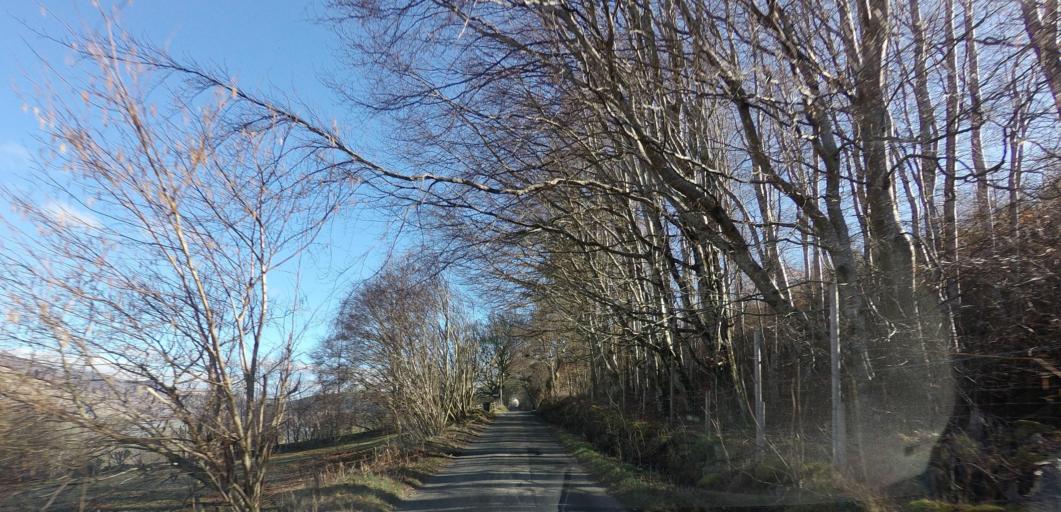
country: GB
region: Scotland
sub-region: Perth and Kinross
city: Comrie
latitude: 56.5516
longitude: -4.0909
